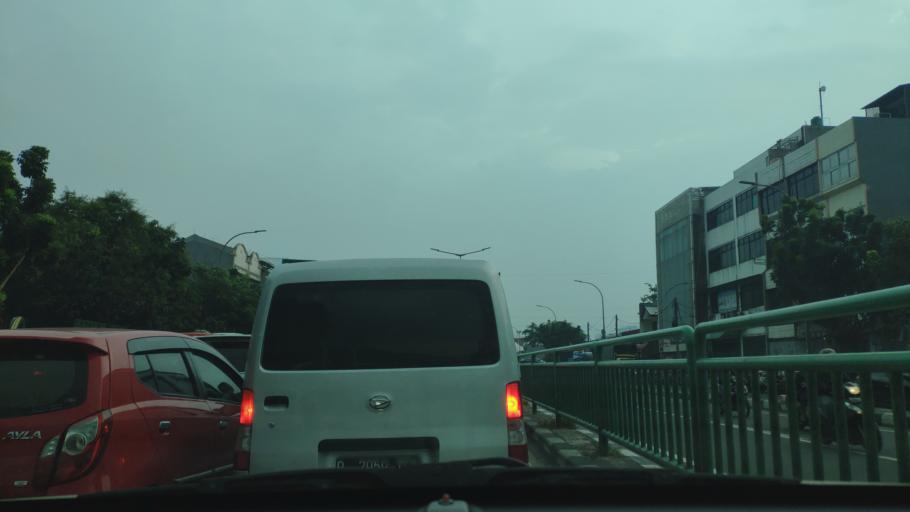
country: ID
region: Jakarta Raya
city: Jakarta
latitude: -6.1830
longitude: 106.8128
